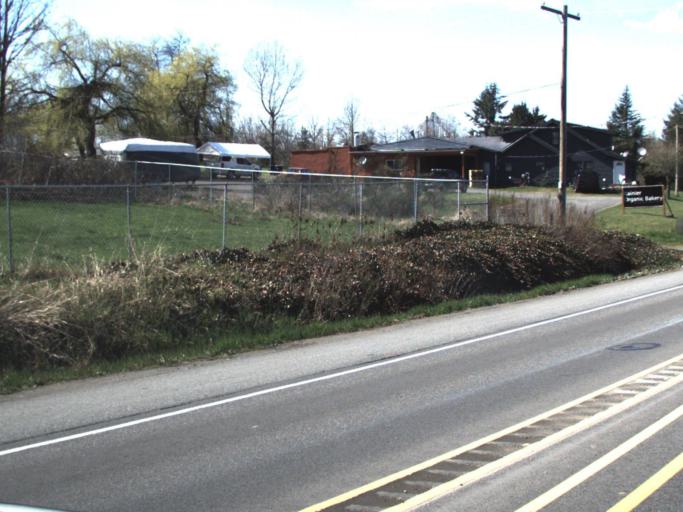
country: US
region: Washington
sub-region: King County
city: Lake Morton-Berrydale
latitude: 47.2546
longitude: -122.1216
